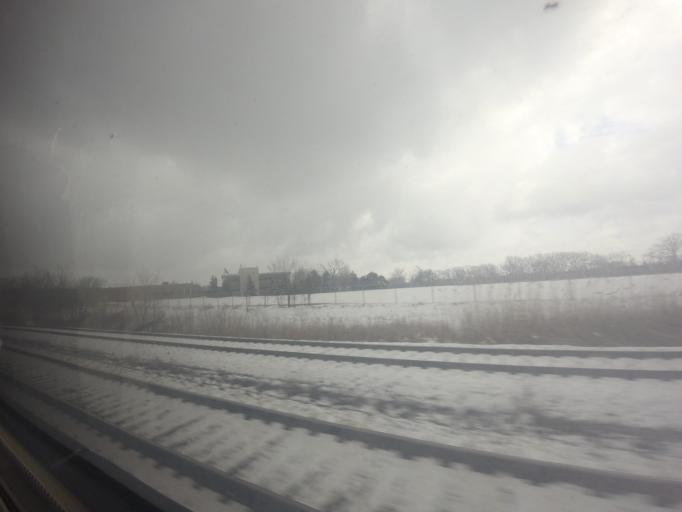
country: CA
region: Ontario
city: Scarborough
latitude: 43.6969
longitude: -79.2686
